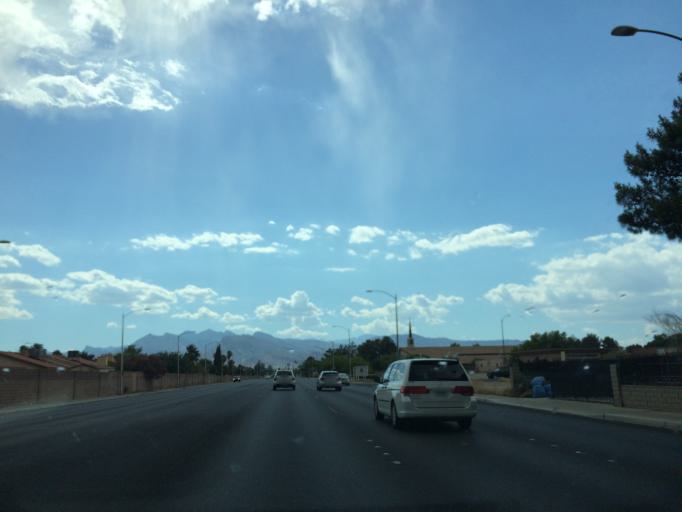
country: US
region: Nevada
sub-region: Clark County
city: Las Vegas
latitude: 36.2172
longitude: -115.2288
